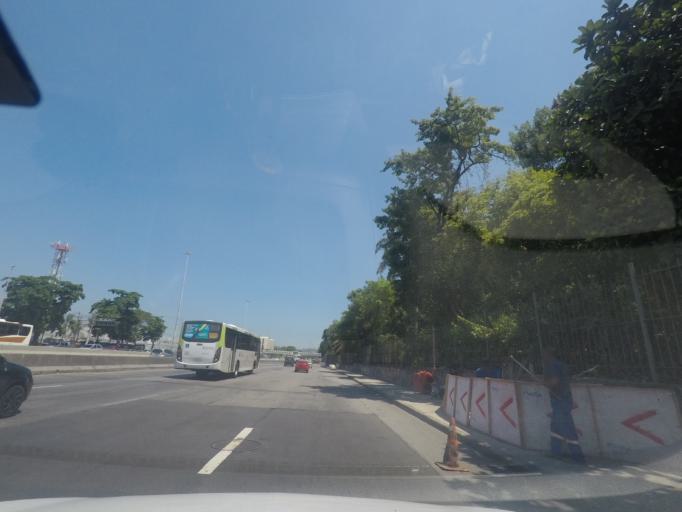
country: BR
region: Rio de Janeiro
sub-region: Rio De Janeiro
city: Rio de Janeiro
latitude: -22.8726
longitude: -43.2455
